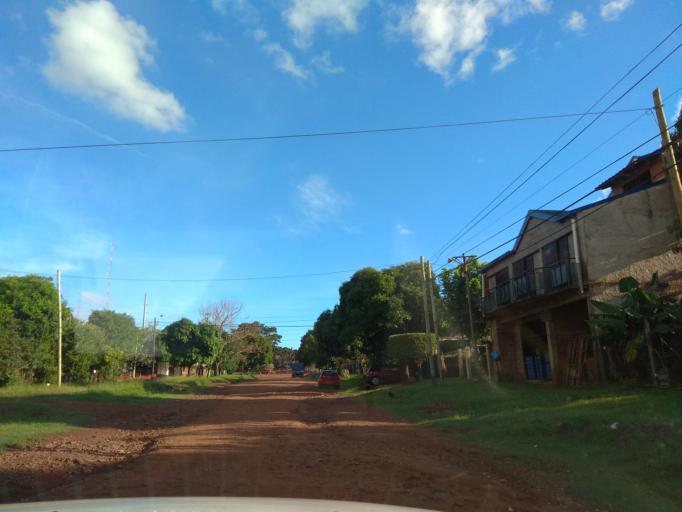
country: AR
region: Misiones
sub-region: Departamento de Capital
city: Posadas
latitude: -27.4000
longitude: -55.9287
